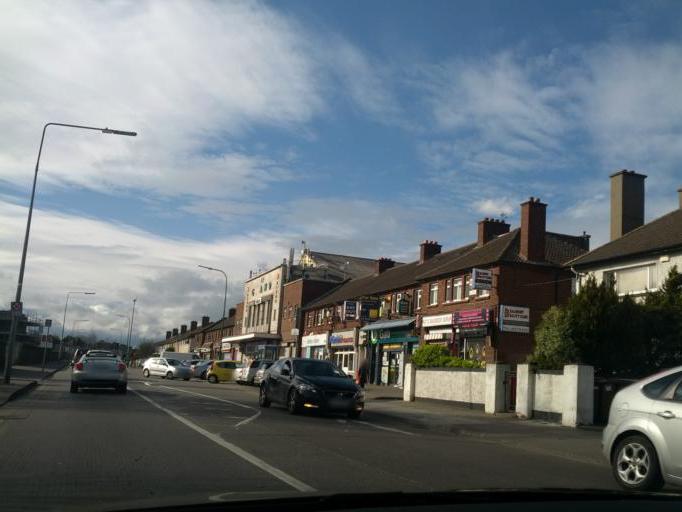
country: IE
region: Leinster
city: Beaumont
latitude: 53.3812
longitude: -6.2400
